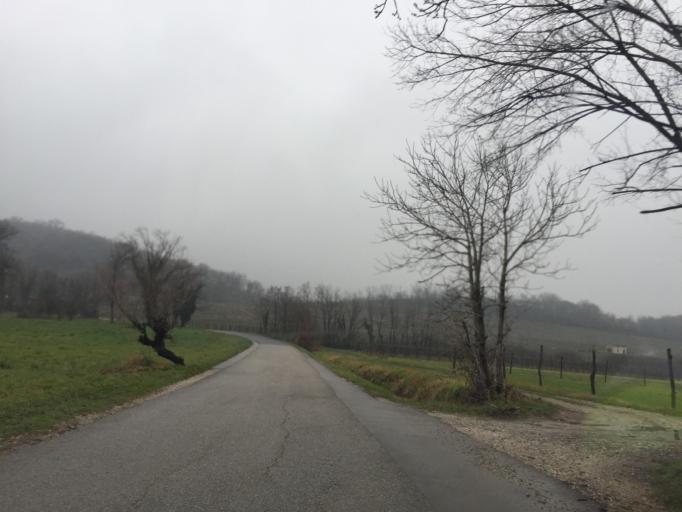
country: SI
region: Ajdovscina
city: Lokavec
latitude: 45.8904
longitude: 13.8683
